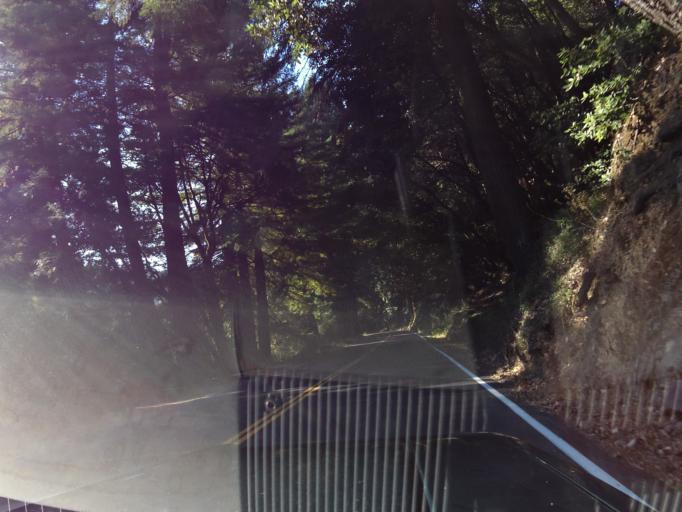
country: US
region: California
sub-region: Mendocino County
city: Boonville
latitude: 39.1623
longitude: -123.6387
